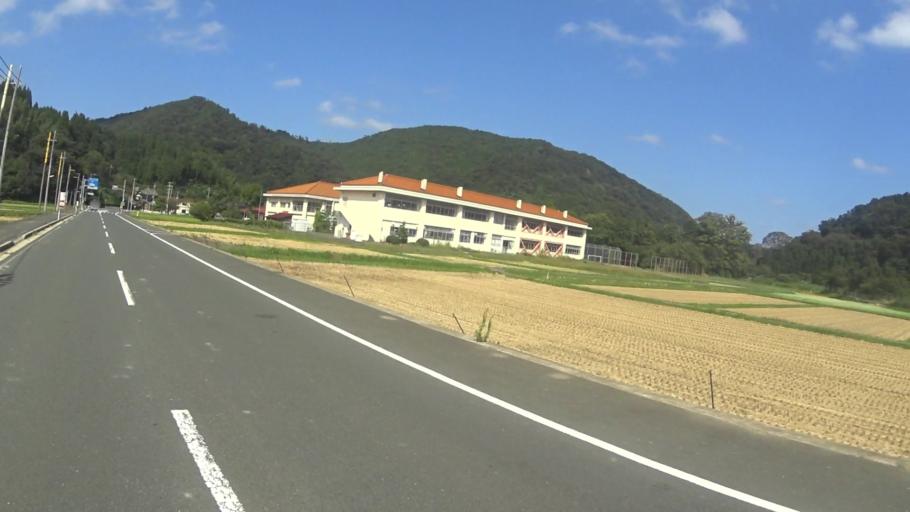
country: JP
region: Kyoto
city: Miyazu
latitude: 35.7276
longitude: 135.2554
